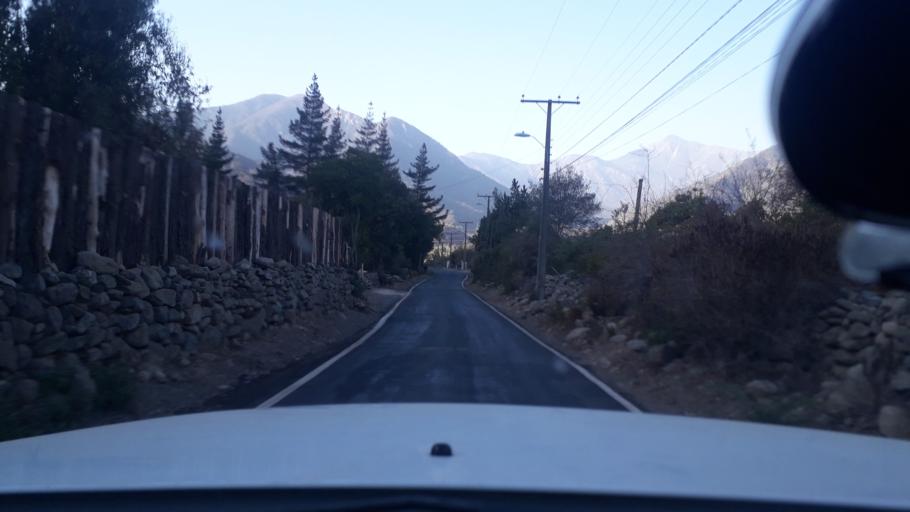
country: CL
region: Valparaiso
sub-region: Provincia de Marga Marga
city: Limache
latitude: -33.0574
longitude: -71.1139
